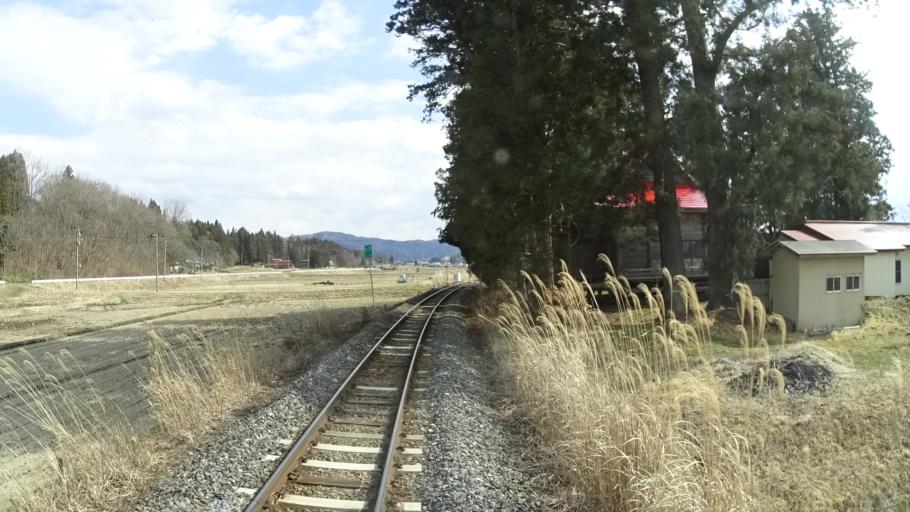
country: JP
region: Iwate
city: Hanamaki
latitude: 39.3728
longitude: 141.2549
